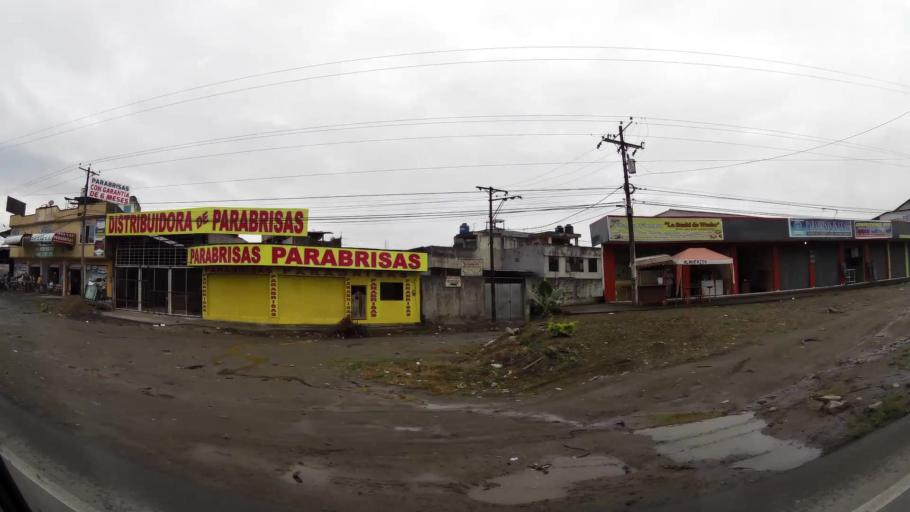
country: EC
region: Santo Domingo de los Tsachilas
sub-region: Canton Santo Domingo de los Colorados
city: Santo Domingo de los Colorados
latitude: -0.2447
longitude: -79.1984
